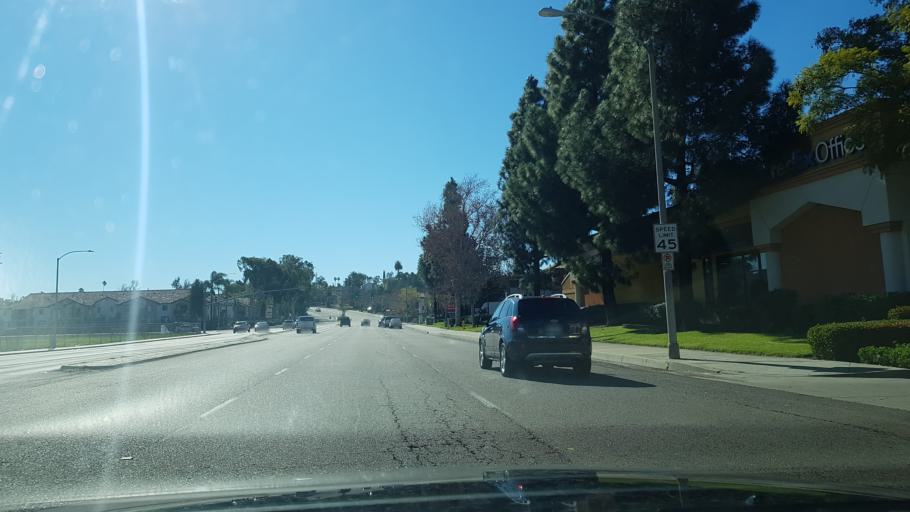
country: US
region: California
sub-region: San Diego County
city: Escondido
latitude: 33.1120
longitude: -117.1028
